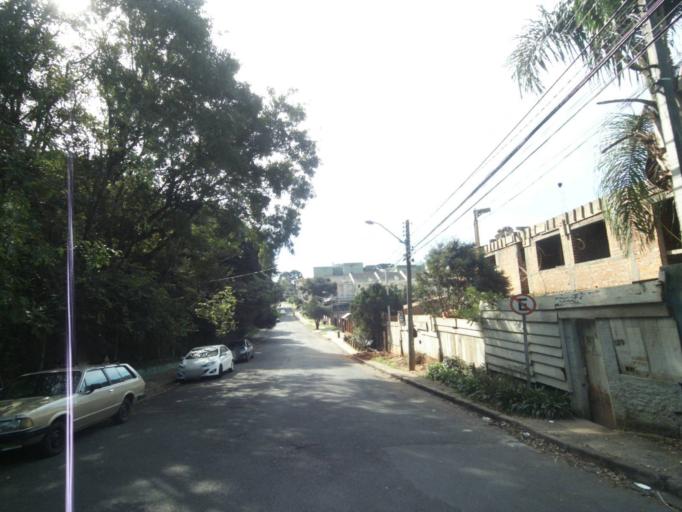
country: BR
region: Parana
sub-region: Curitiba
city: Curitiba
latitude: -25.4191
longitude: -49.2924
